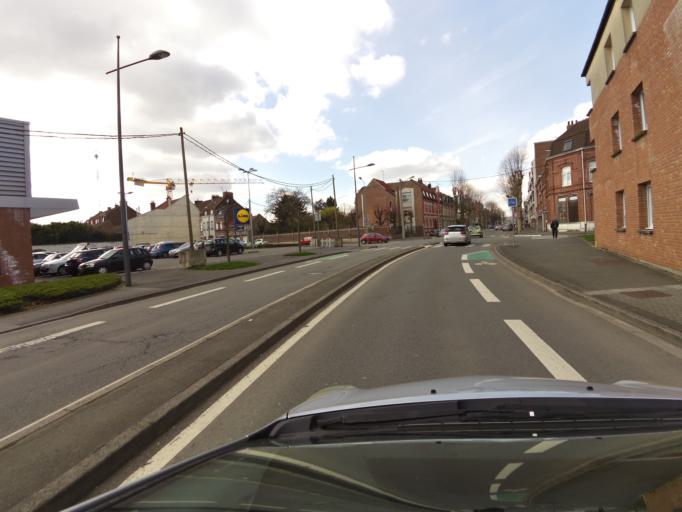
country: FR
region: Nord-Pas-de-Calais
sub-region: Departement du Nord
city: Armentieres
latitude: 50.6826
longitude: 2.8717
